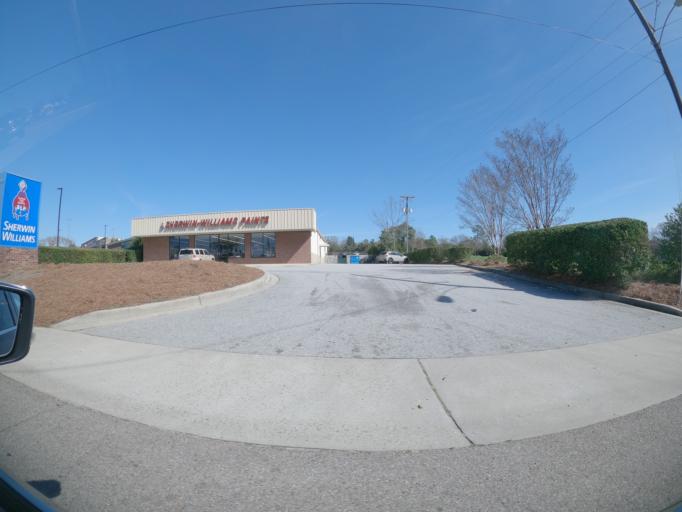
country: US
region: South Carolina
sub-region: Aiken County
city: North Augusta
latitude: 33.4957
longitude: -81.9582
